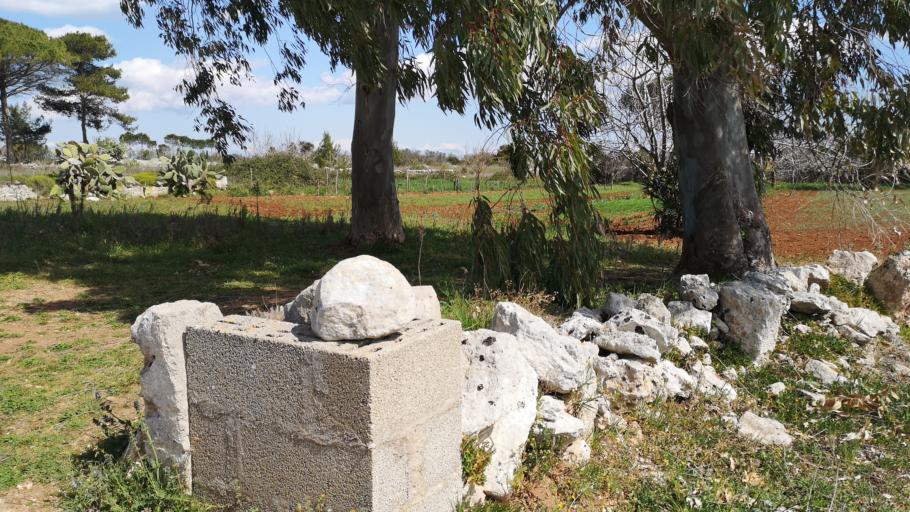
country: IT
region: Apulia
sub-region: Provincia di Lecce
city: Spongano
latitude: 40.0276
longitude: 18.3624
